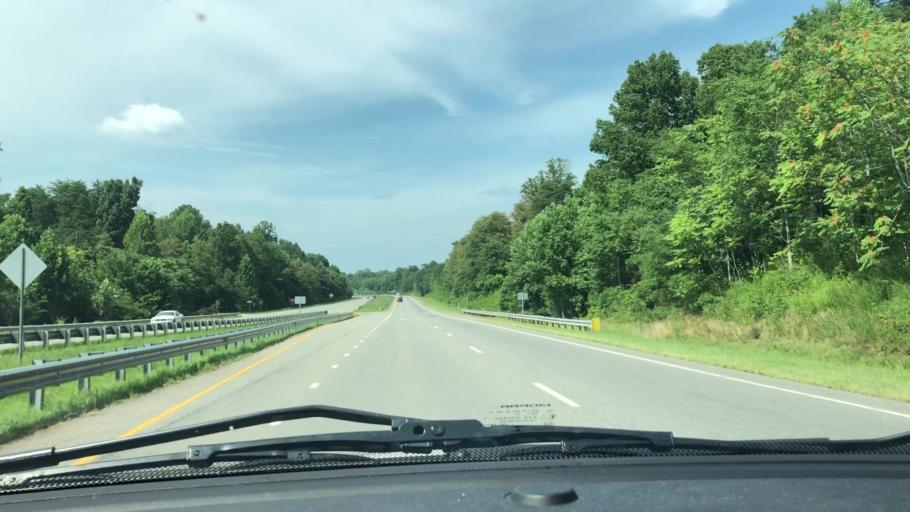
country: US
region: North Carolina
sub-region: Rockingham County
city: Stoneville
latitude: 36.5087
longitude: -79.9198
